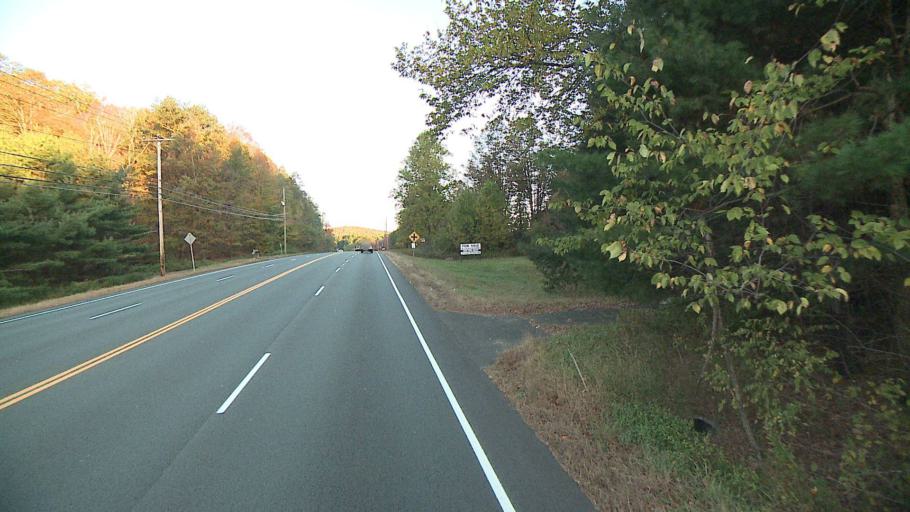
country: US
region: Connecticut
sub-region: Hartford County
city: Canton Valley
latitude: 41.8199
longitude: -72.8714
